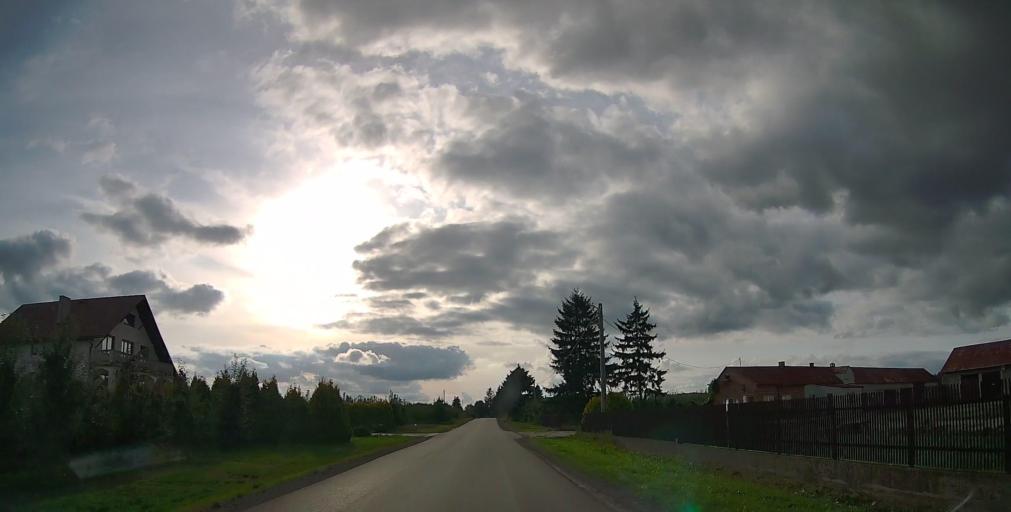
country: PL
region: Masovian Voivodeship
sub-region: Powiat grojecki
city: Jasieniec
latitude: 51.7583
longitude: 20.9412
